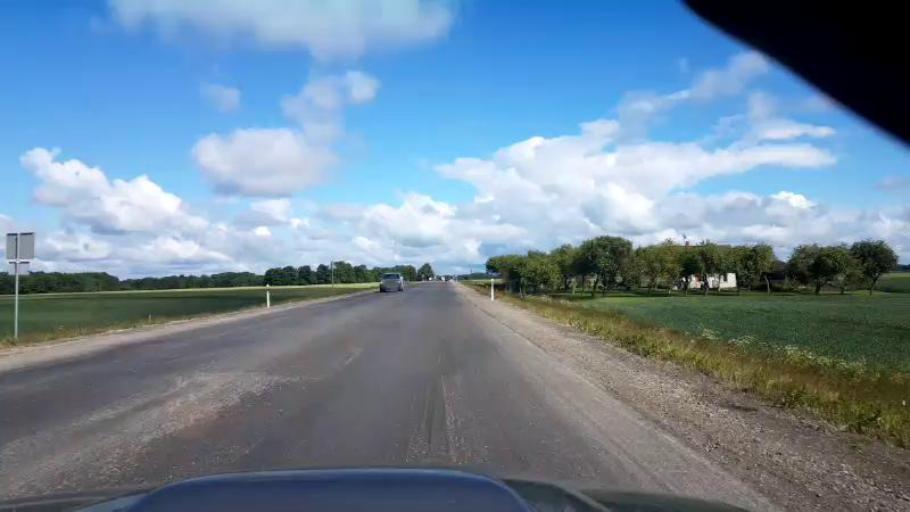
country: LV
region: Bauskas Rajons
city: Bauska
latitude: 56.3845
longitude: 24.2564
